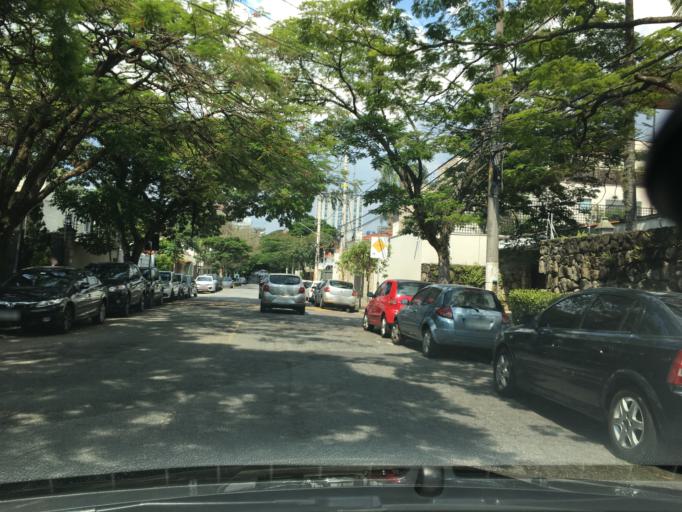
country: BR
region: Sao Paulo
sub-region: Sao Paulo
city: Sao Paulo
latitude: -23.5764
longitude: -46.6943
